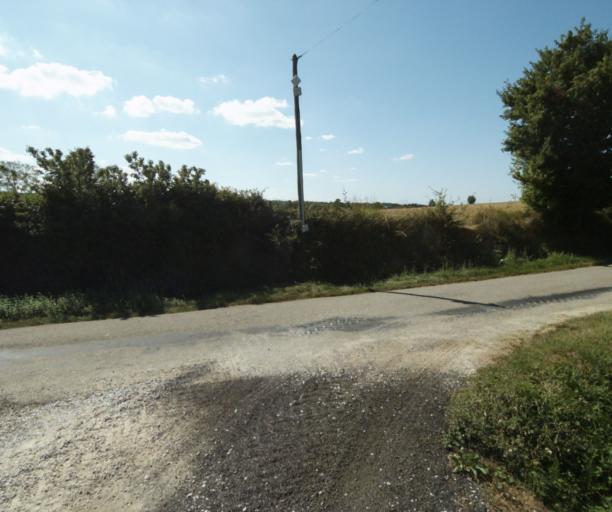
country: FR
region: Midi-Pyrenees
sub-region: Departement de la Haute-Garonne
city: Saint-Felix-Lauragais
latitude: 43.4747
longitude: 1.8938
